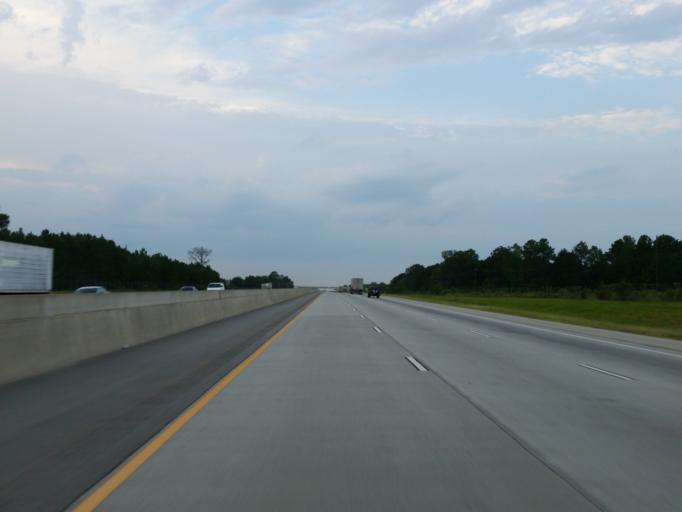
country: US
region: Georgia
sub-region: Tift County
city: Omega
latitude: 31.3235
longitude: -83.4810
